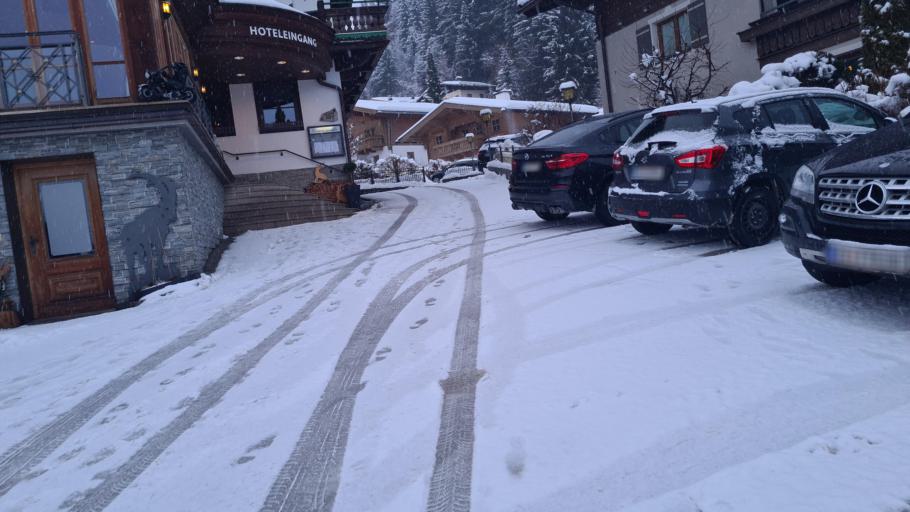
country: AT
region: Salzburg
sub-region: Politischer Bezirk Zell am See
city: Neukirchen am Grossvenediger
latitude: 47.2543
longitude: 12.2721
